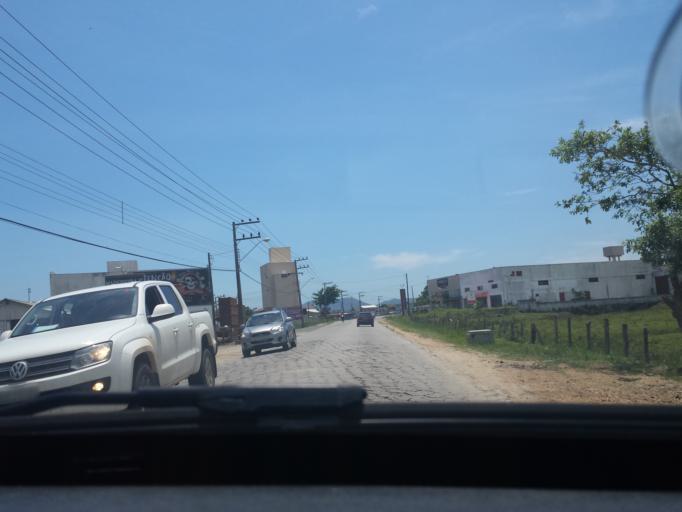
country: BR
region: Santa Catarina
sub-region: Porto Belo
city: Porto Belo
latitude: -27.1576
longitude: -48.5929
